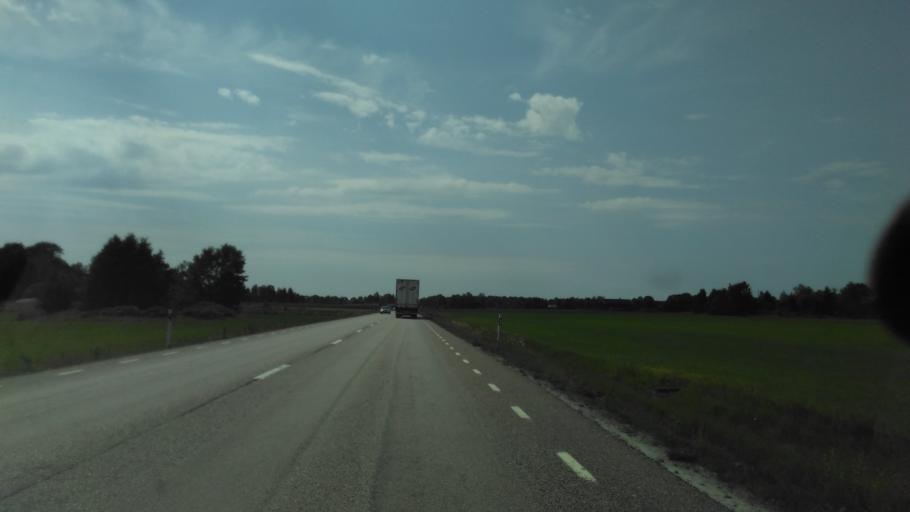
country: SE
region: Vaestra Goetaland
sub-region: Grastorps Kommun
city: Graestorp
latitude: 58.4090
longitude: 12.8378
